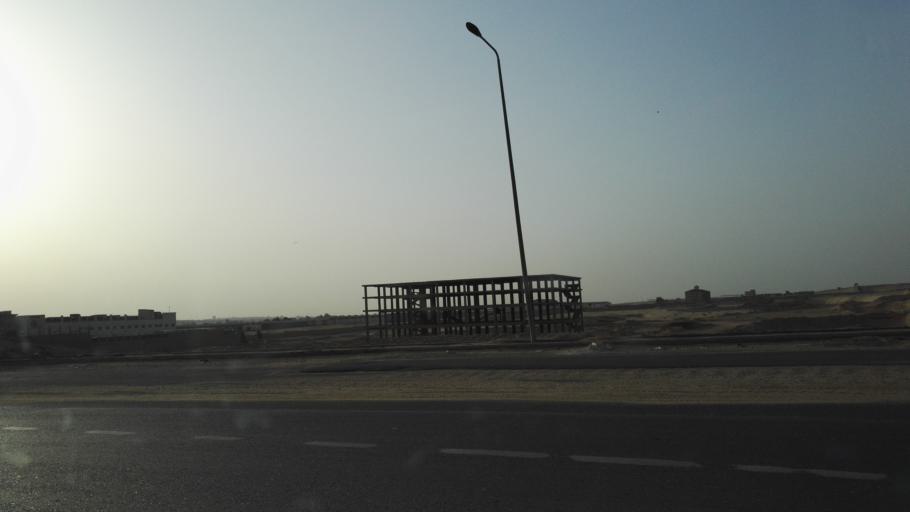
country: EG
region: Muhafazat al Qahirah
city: Cairo
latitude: 29.9889
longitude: 31.3701
